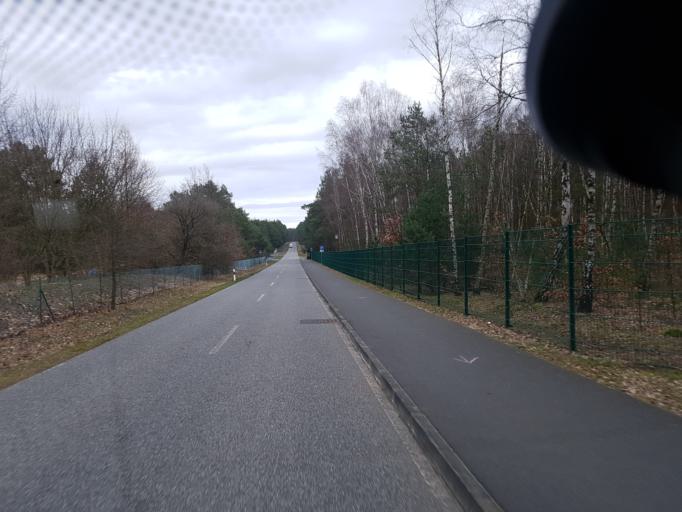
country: DE
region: Brandenburg
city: Mixdorf
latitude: 52.1848
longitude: 14.4421
